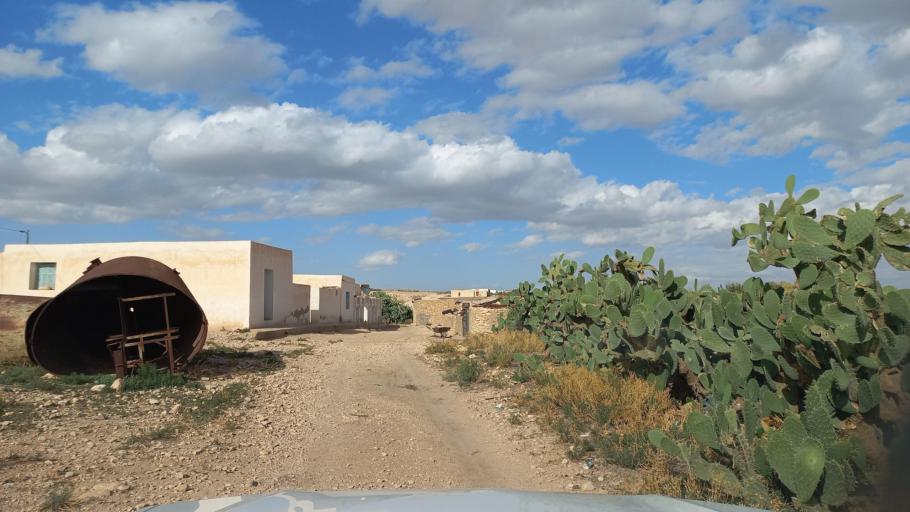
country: TN
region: Al Qasrayn
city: Sbiba
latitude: 35.4523
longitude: 9.0764
